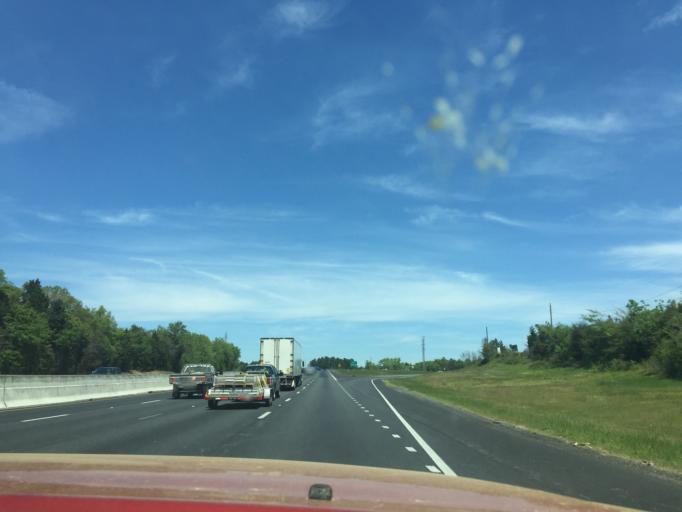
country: US
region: North Carolina
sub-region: Mecklenburg County
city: Pineville
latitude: 35.0875
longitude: -80.9365
